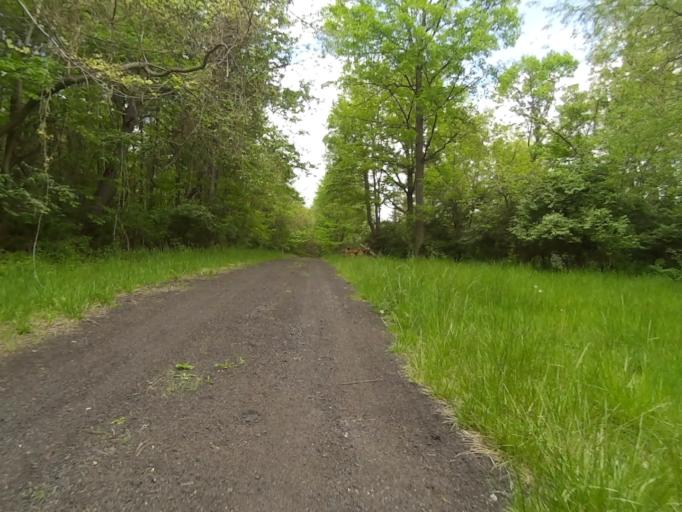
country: US
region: Pennsylvania
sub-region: Centre County
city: Park Forest Village
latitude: 40.8353
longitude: -77.9071
